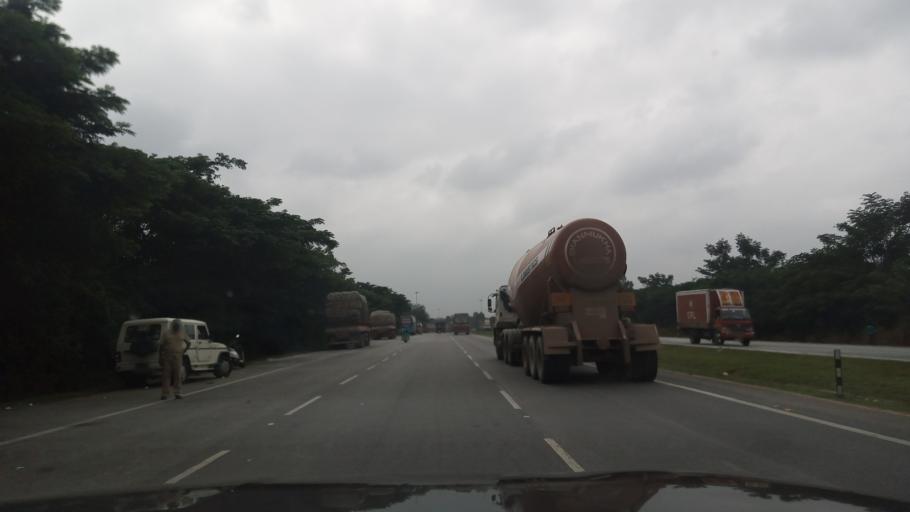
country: IN
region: Karnataka
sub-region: Bangalore Rural
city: Nelamangala
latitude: 13.0496
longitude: 77.4762
